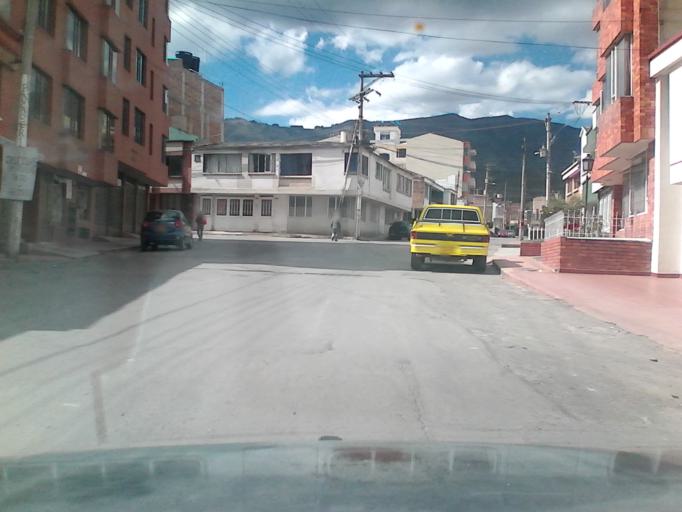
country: CO
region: Boyaca
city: Duitama
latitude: 5.8337
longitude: -73.0359
